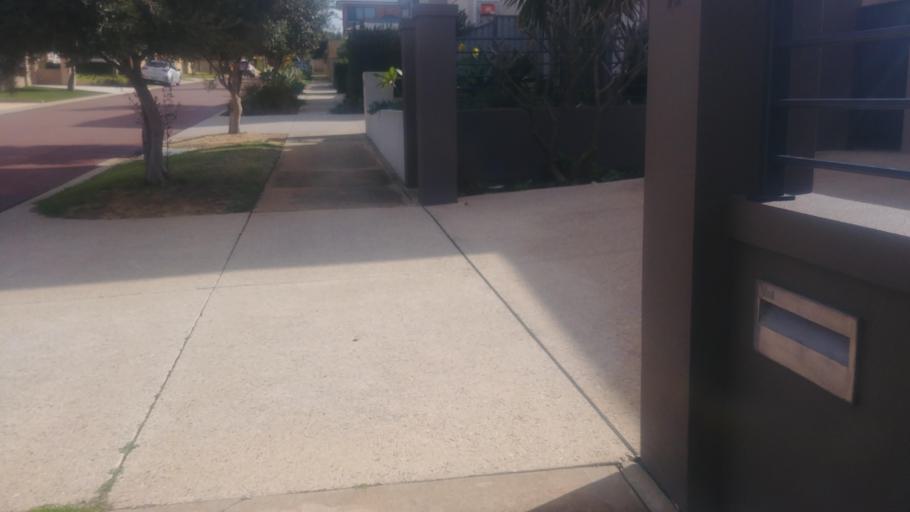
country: AU
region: Western Australia
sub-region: Fremantle
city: South Fremantle
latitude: -32.0682
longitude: 115.7638
